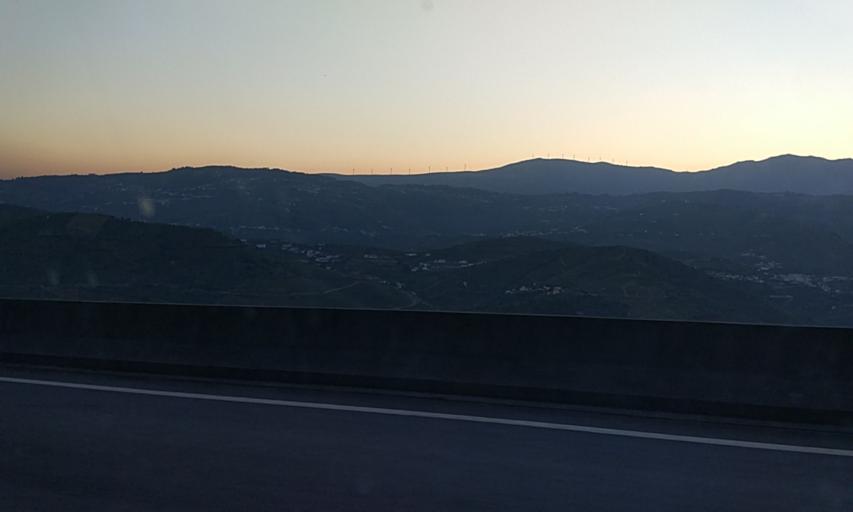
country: PT
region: Vila Real
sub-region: Peso da Regua
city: Peso da Regua
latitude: 41.1987
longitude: -7.7473
